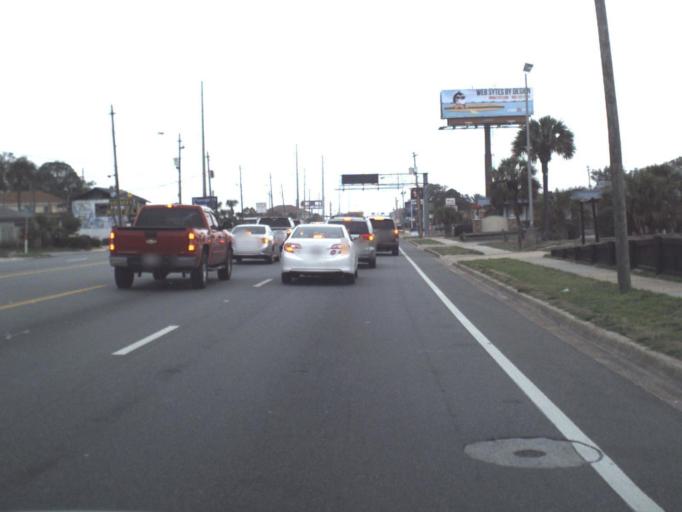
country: US
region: Florida
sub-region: Bay County
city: Upper Grand Lagoon
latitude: 30.1818
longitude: -85.7234
